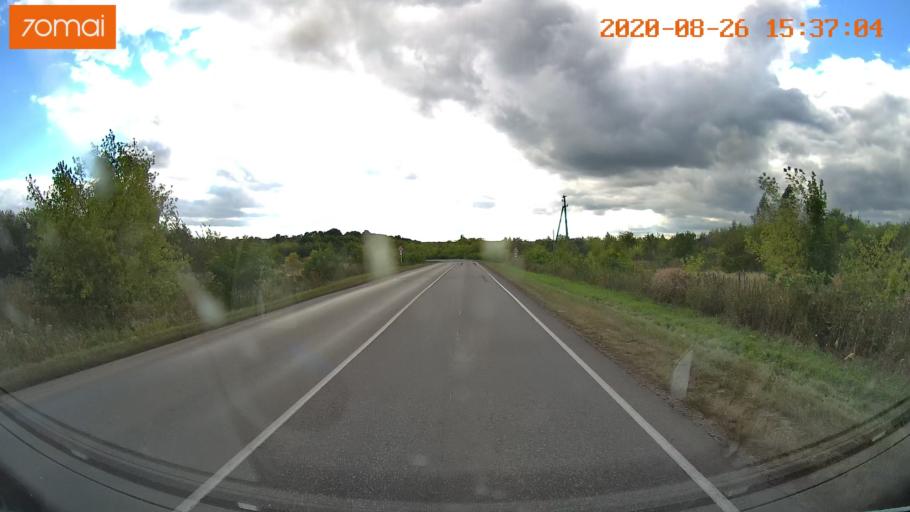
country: RU
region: Tula
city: Severo-Zadonsk
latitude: 54.0380
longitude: 38.3613
